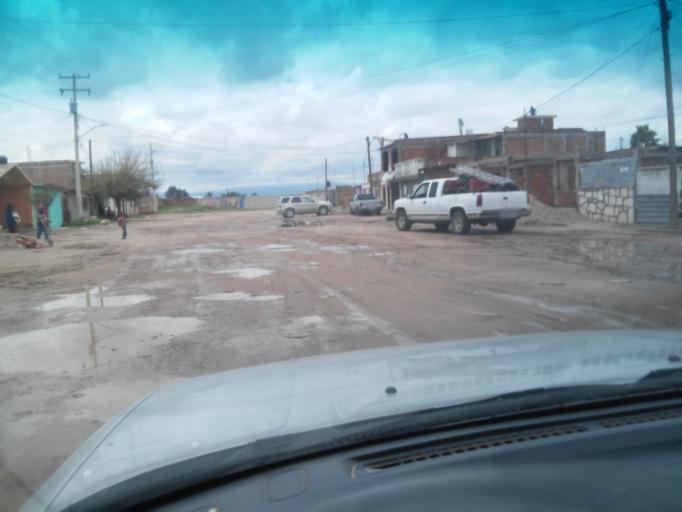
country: MX
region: Durango
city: Victoria de Durango
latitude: 24.0120
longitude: -104.6224
